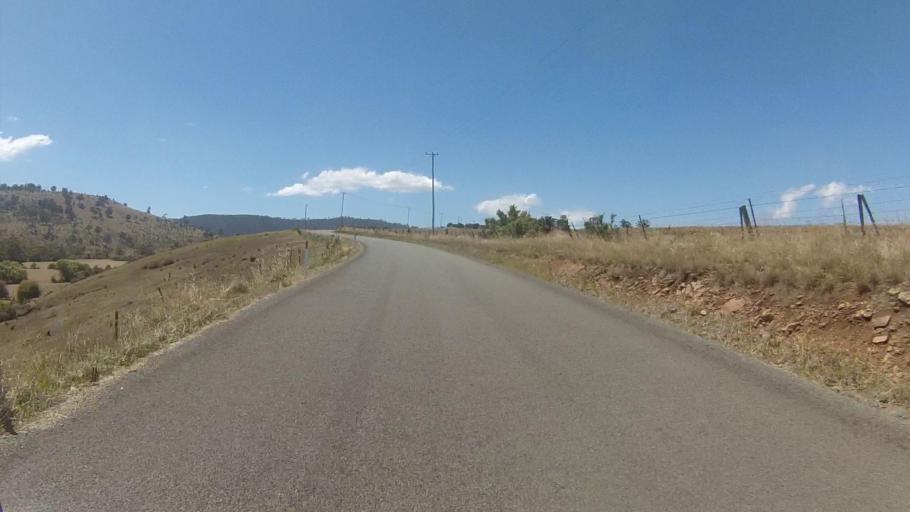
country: AU
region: Tasmania
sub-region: Sorell
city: Sorell
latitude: -42.7700
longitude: 147.5951
